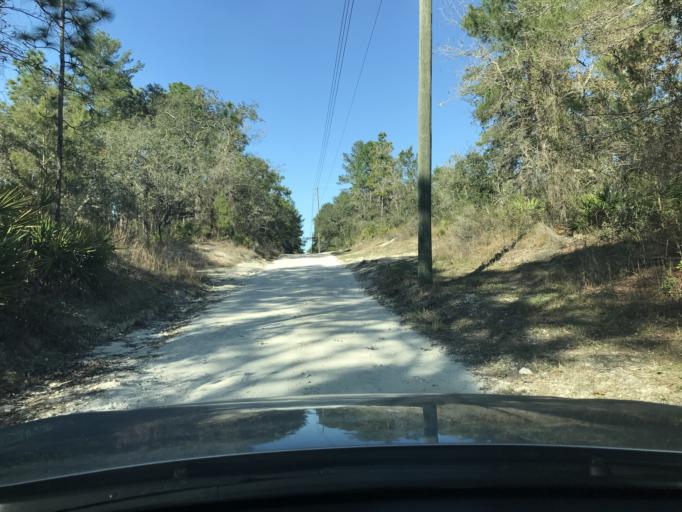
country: US
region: Florida
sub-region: Hernando County
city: North Weeki Wachee
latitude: 28.5497
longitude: -82.5662
